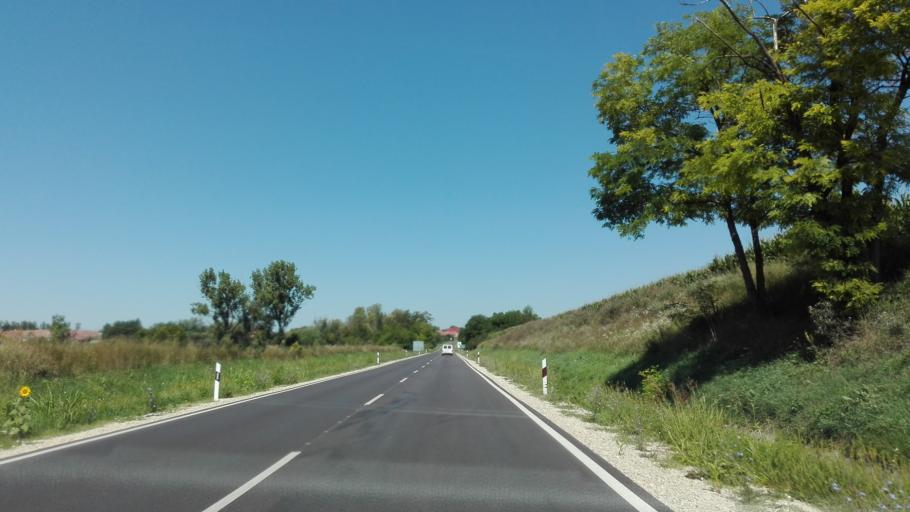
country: HU
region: Tolna
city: Simontornya
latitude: 46.7666
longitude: 18.5212
